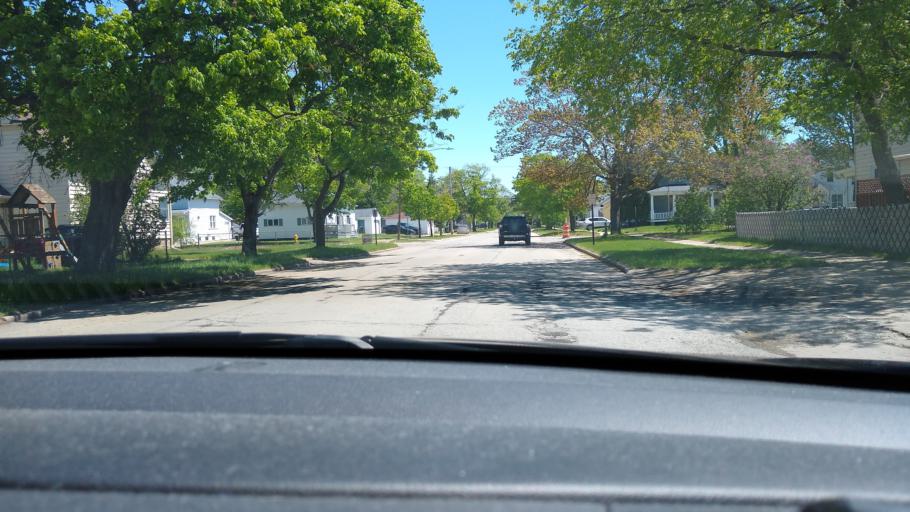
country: US
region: Michigan
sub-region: Delta County
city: Escanaba
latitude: 45.7395
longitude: -87.0707
